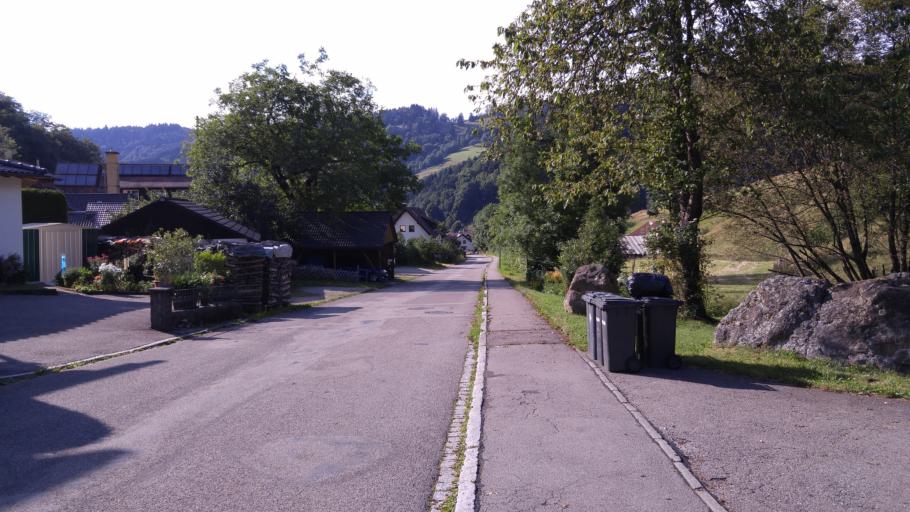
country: DE
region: Baden-Wuerttemberg
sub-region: Freiburg Region
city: Wieden
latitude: 47.8733
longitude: 7.8433
